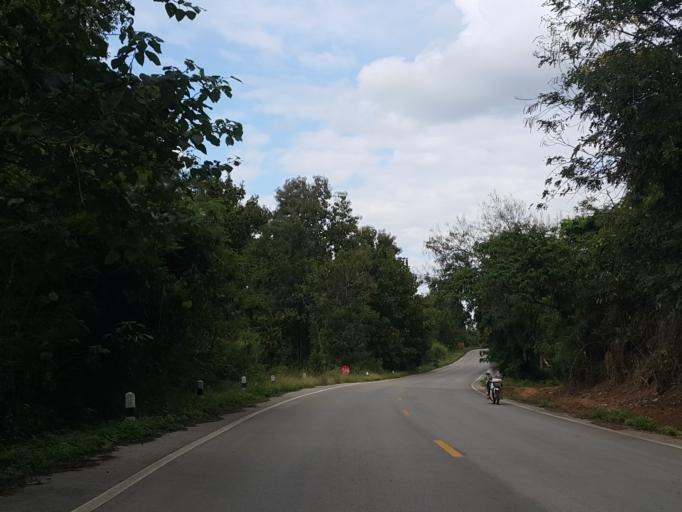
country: TH
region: Lampang
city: Chae Hom
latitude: 18.6295
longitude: 99.4905
